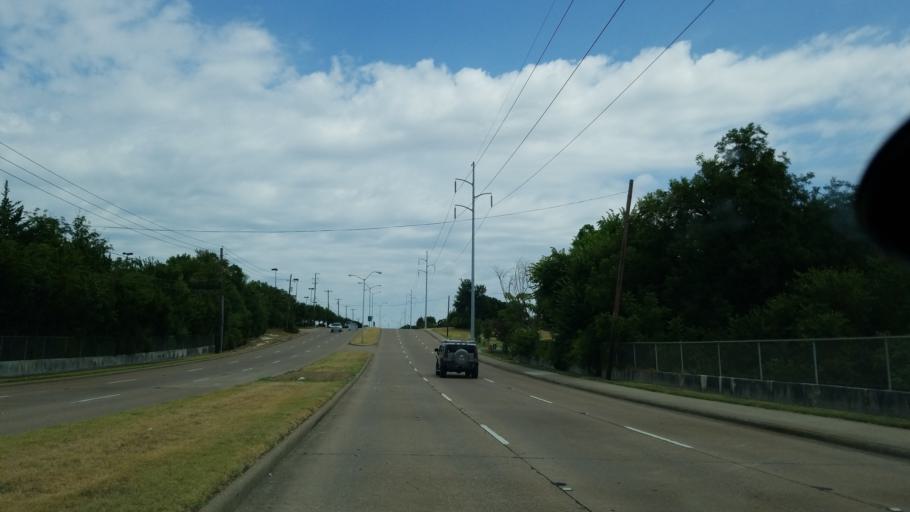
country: US
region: Texas
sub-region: Dallas County
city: Duncanville
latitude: 32.6621
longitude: -96.8452
